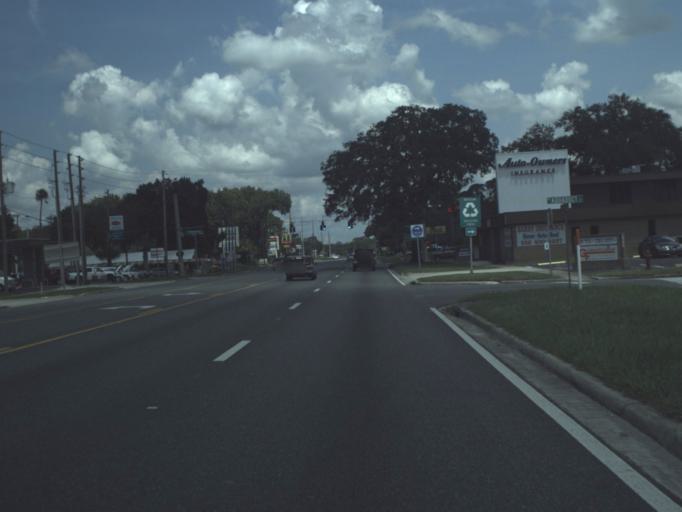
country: US
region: Florida
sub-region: Citrus County
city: Homosassa Springs
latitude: 28.8043
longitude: -82.5763
